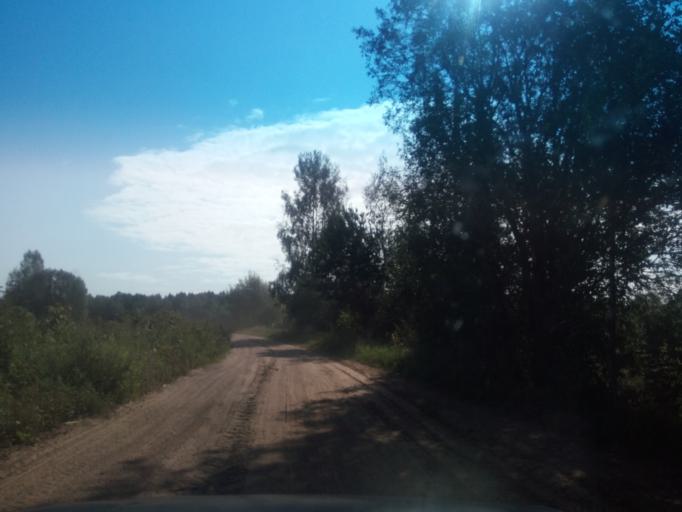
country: BY
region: Vitebsk
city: Dzisna
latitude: 55.6432
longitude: 28.2916
